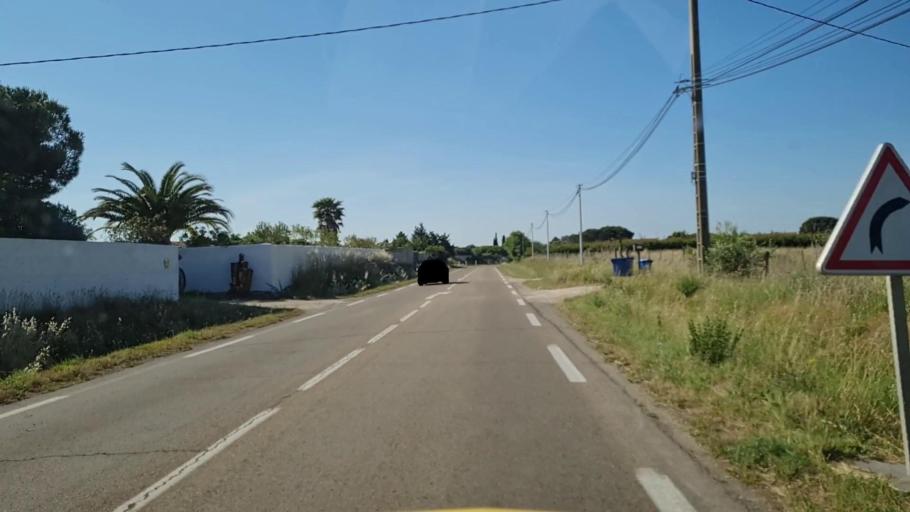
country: FR
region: Languedoc-Roussillon
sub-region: Departement du Gard
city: Saint-Gilles
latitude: 43.6926
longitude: 4.4269
